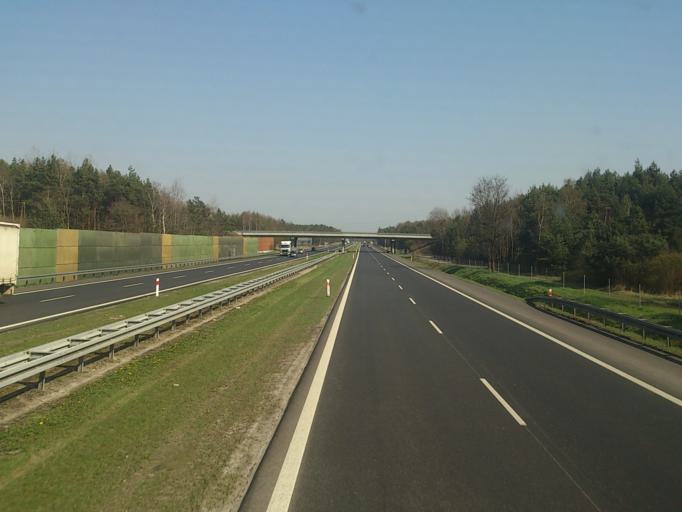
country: PL
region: Lesser Poland Voivodeship
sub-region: Powiat chrzanowski
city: Trzebinia
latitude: 50.1444
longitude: 19.4414
